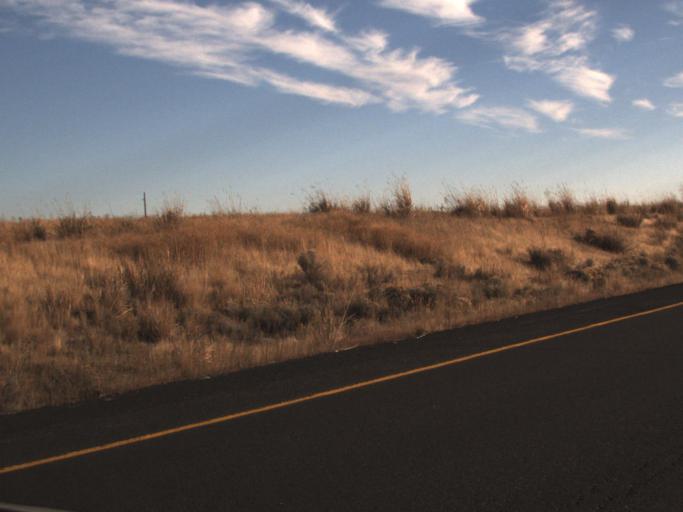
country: US
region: Washington
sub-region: Adams County
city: Ritzville
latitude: 47.1074
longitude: -118.3977
